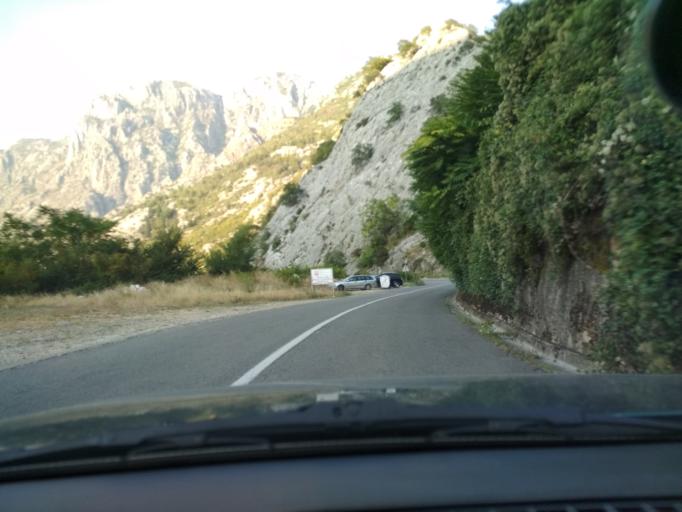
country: ME
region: Kotor
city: Kotor
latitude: 42.4079
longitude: 18.7682
